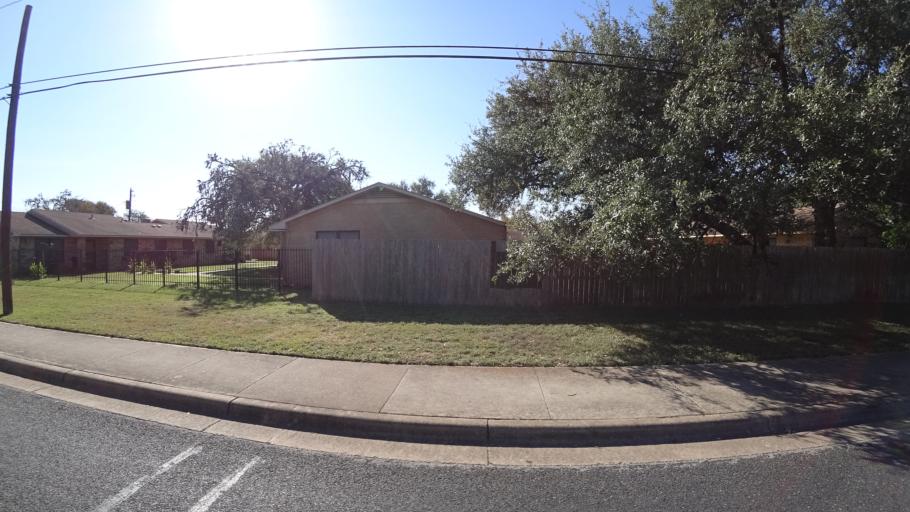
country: US
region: Texas
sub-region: Travis County
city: Barton Creek
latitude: 30.2342
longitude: -97.8510
